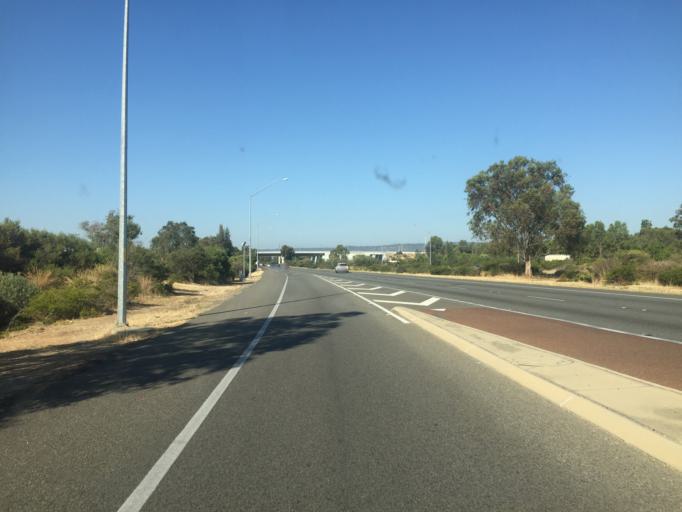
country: AU
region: Western Australia
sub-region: Gosnells
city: Kenwick
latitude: -32.0353
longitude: 115.9616
